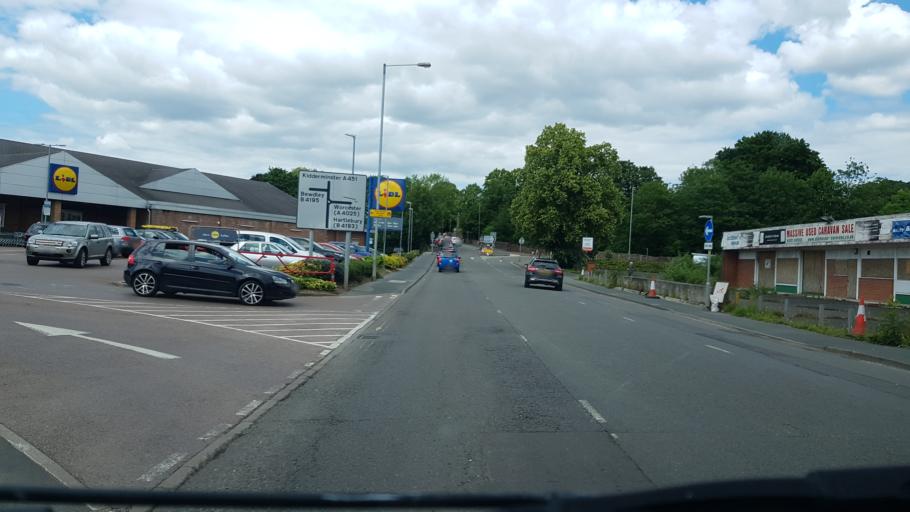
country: GB
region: England
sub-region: Worcestershire
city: Stourport-on-Severn
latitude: 52.3419
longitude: -2.2762
